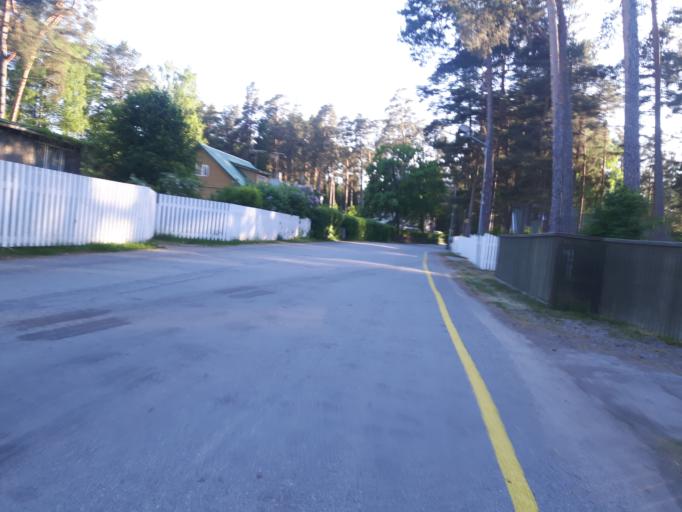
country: EE
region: Harju
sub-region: Loksa linn
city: Loksa
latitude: 59.5752
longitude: 25.9565
